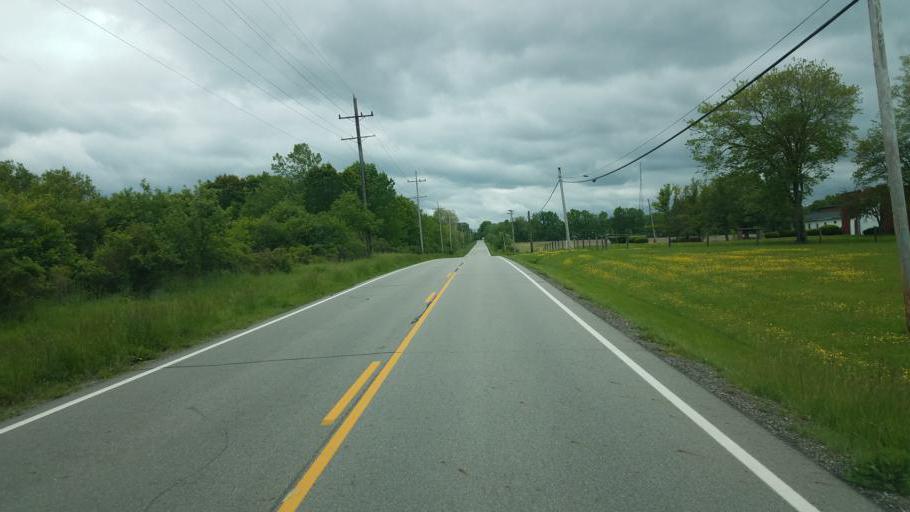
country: US
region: Ohio
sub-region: Geauga County
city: Burton
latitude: 41.4000
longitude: -81.1717
